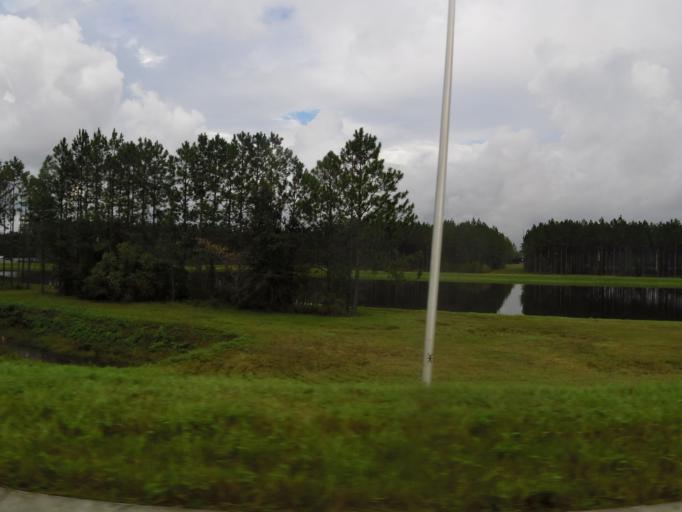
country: US
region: Florida
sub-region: Duval County
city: Baldwin
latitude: 30.3042
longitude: -81.8781
